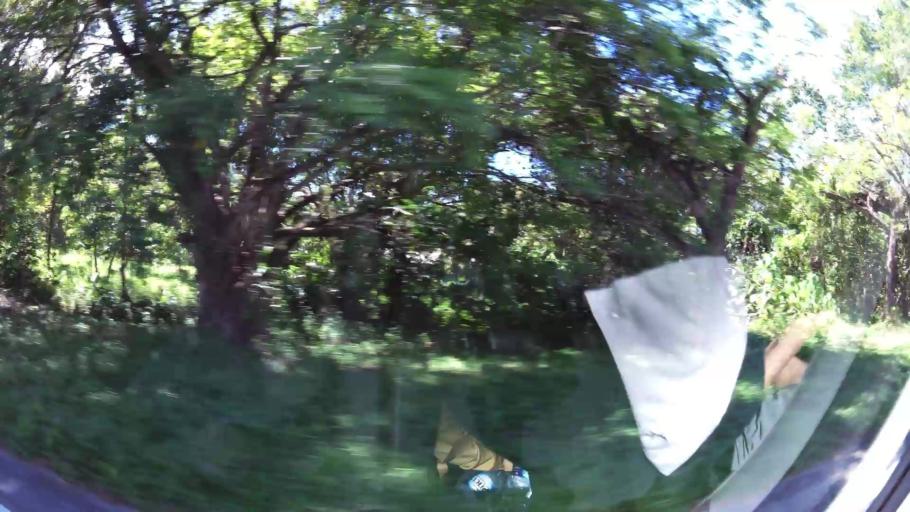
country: BN
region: Brunei and Muara
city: Bandar Seri Begawan
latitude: 5.0332
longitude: 115.0716
